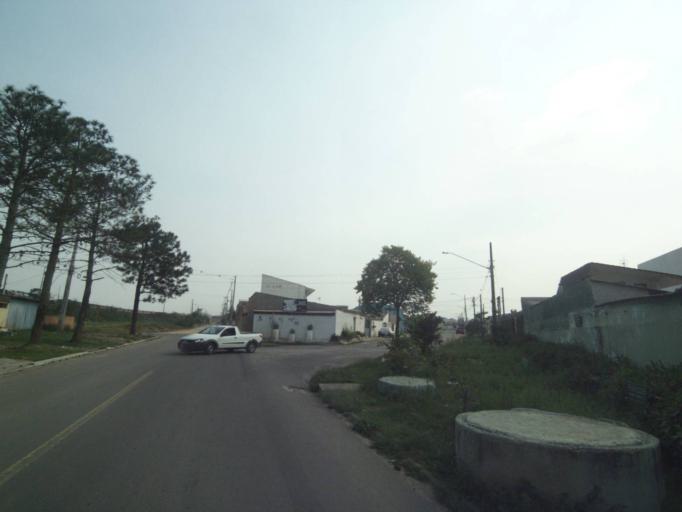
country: BR
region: Parana
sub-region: Sao Jose Dos Pinhais
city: Sao Jose dos Pinhais
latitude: -25.5287
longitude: -49.2297
